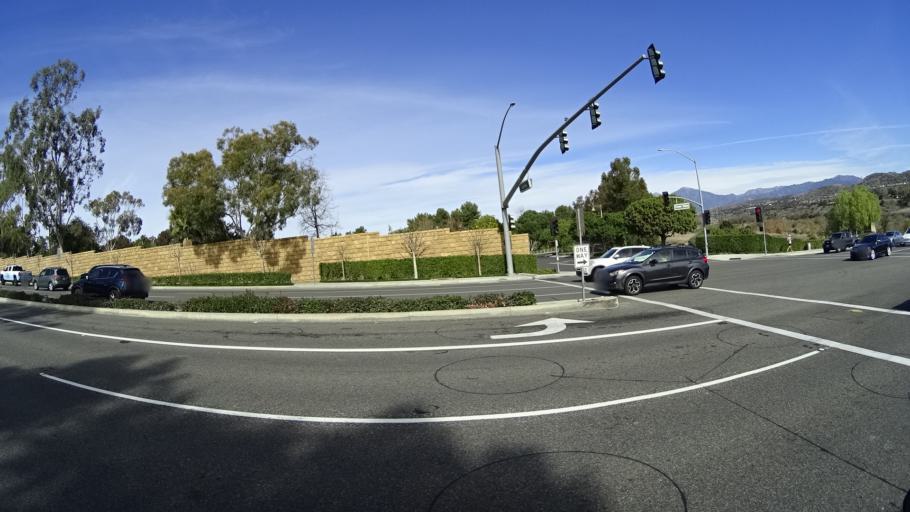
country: US
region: California
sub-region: Orange County
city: Ladera Ranch
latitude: 33.5628
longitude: -117.6553
